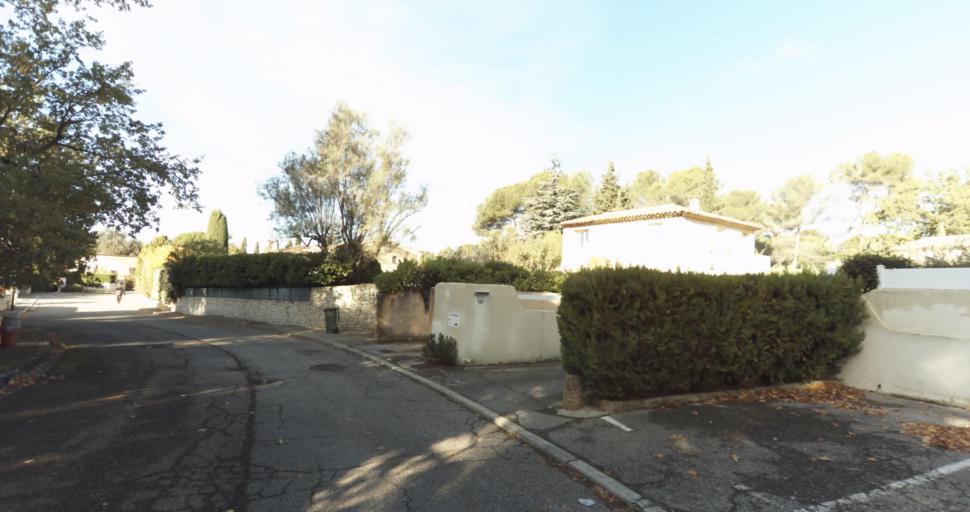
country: FR
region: Provence-Alpes-Cote d'Azur
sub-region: Departement des Bouches-du-Rhone
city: Venelles
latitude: 43.5916
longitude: 5.4678
